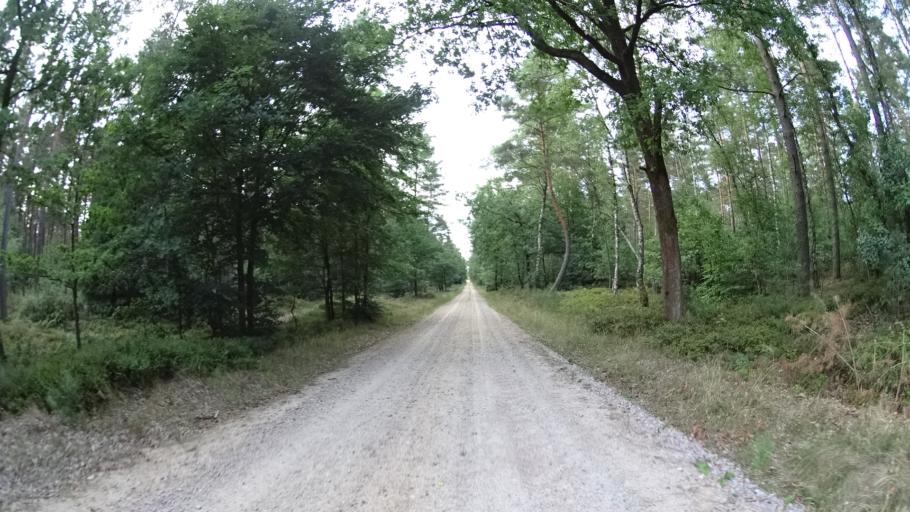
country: DE
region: Lower Saxony
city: Handeloh
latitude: 53.1834
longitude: 9.8843
